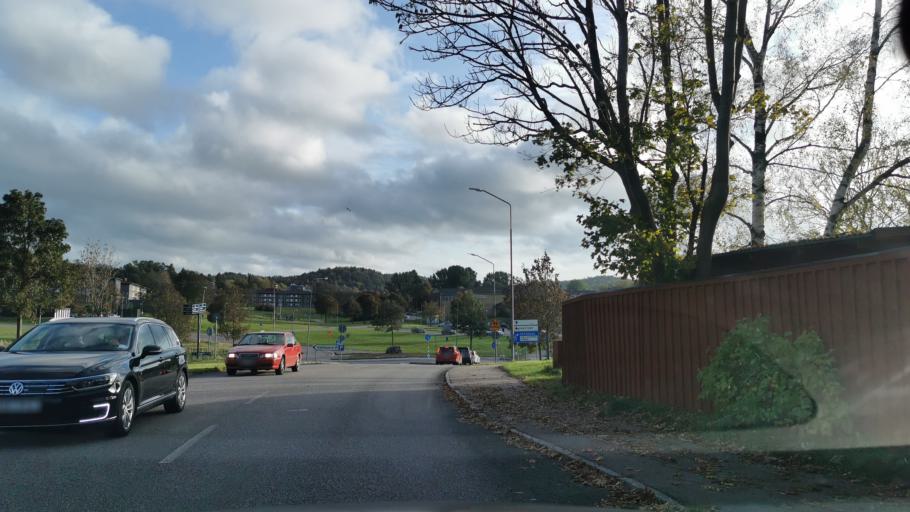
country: SE
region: Vaestra Goetaland
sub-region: Partille Kommun
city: Partille
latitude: 57.7233
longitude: 12.0778
